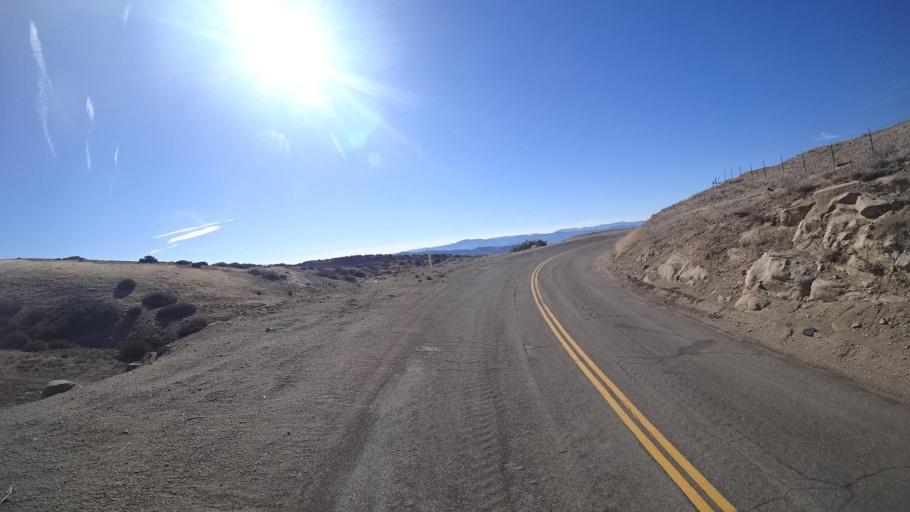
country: US
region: California
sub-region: Kern County
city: Maricopa
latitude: 34.9164
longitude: -119.4099
